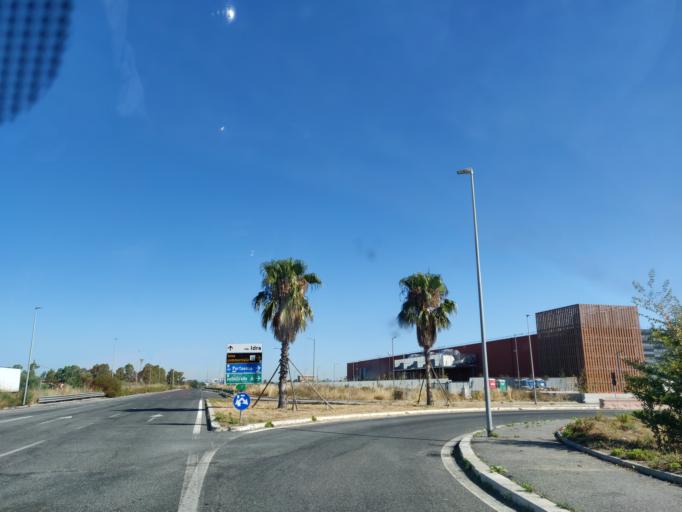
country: IT
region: Latium
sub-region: Citta metropolitana di Roma Capitale
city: Npp 23 (Parco Leonardo)
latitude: 41.8049
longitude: 12.2942
